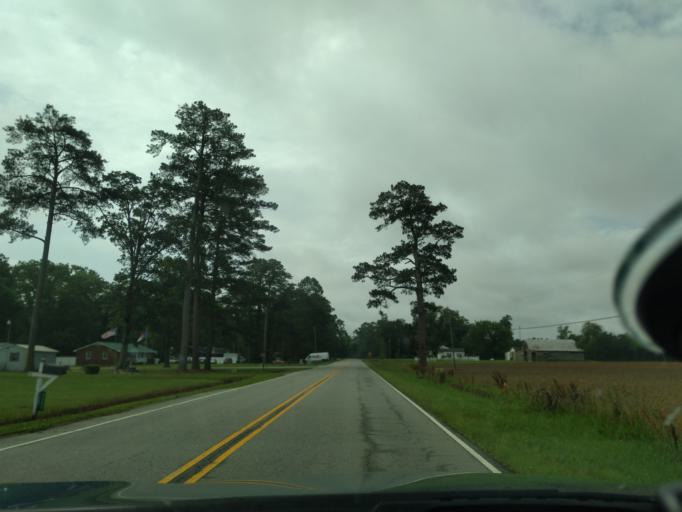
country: US
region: North Carolina
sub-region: Washington County
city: Plymouth
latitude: 35.9003
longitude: -76.6094
